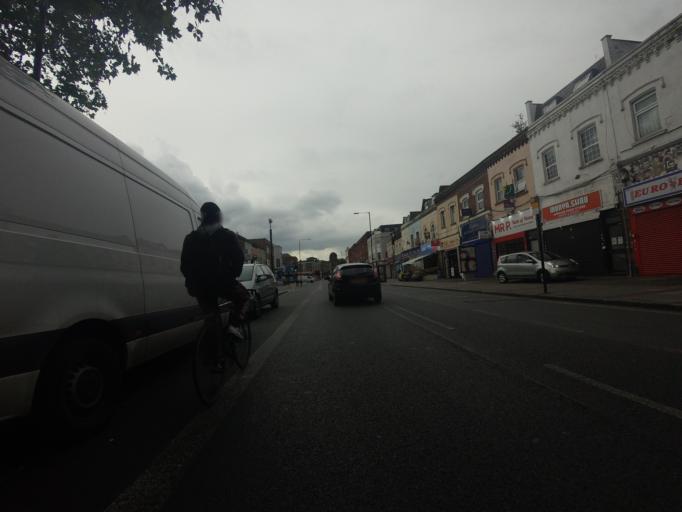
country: GB
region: England
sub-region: Greater London
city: East Ham
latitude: 51.5216
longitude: 0.0209
